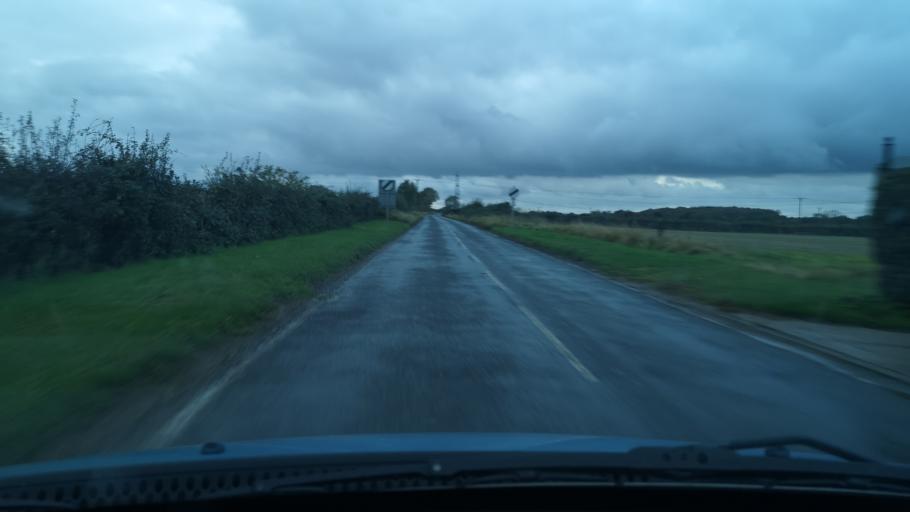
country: GB
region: England
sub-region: Doncaster
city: Norton
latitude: 53.6437
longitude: -1.2236
